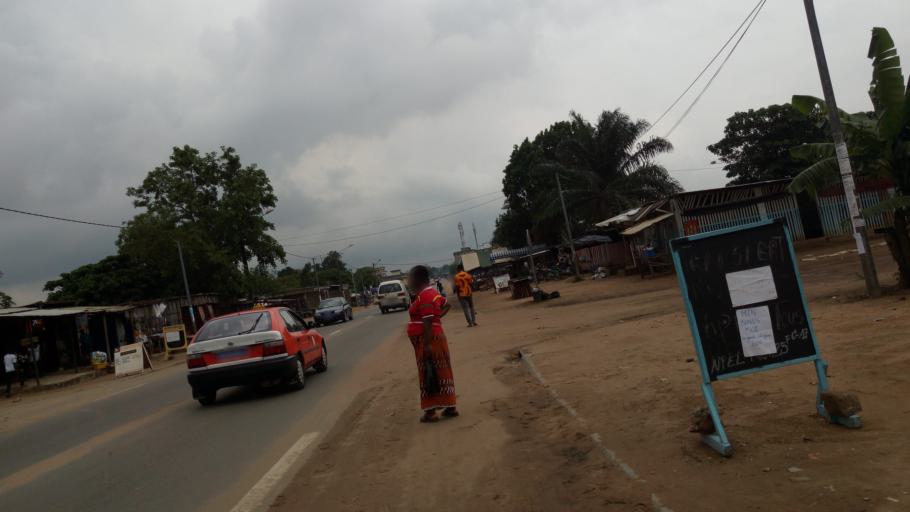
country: CI
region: Lagunes
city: Abobo
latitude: 5.4122
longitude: -3.9961
